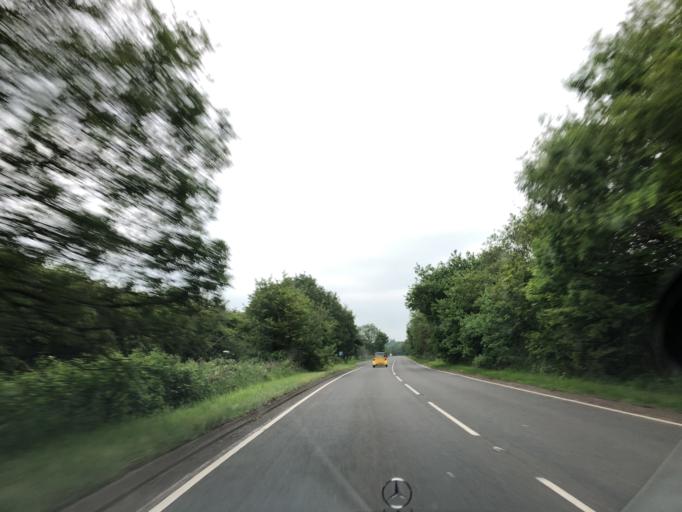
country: GB
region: England
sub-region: Warwickshire
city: Wroxall
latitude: 52.3412
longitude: -1.6586
